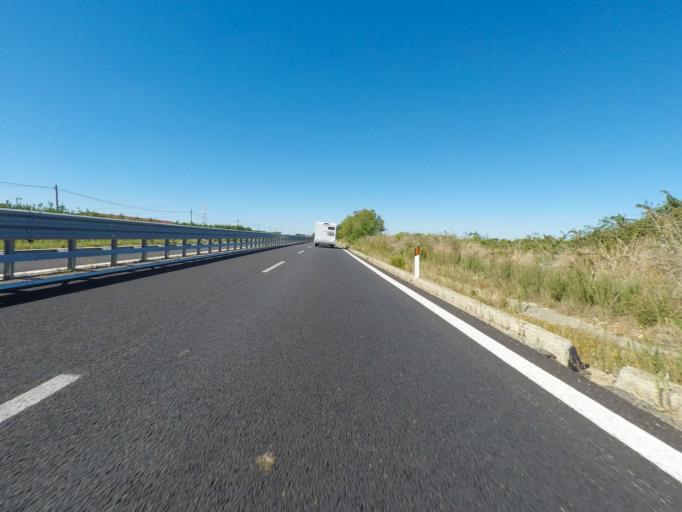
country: IT
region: Latium
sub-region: Provincia di Viterbo
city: Tarquinia
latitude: 42.2748
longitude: 11.7070
